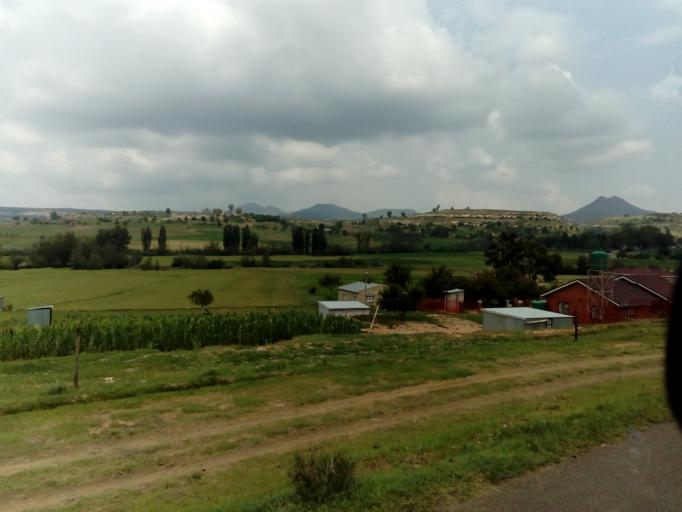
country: LS
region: Leribe
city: Leribe
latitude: -29.0199
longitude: 28.0014
